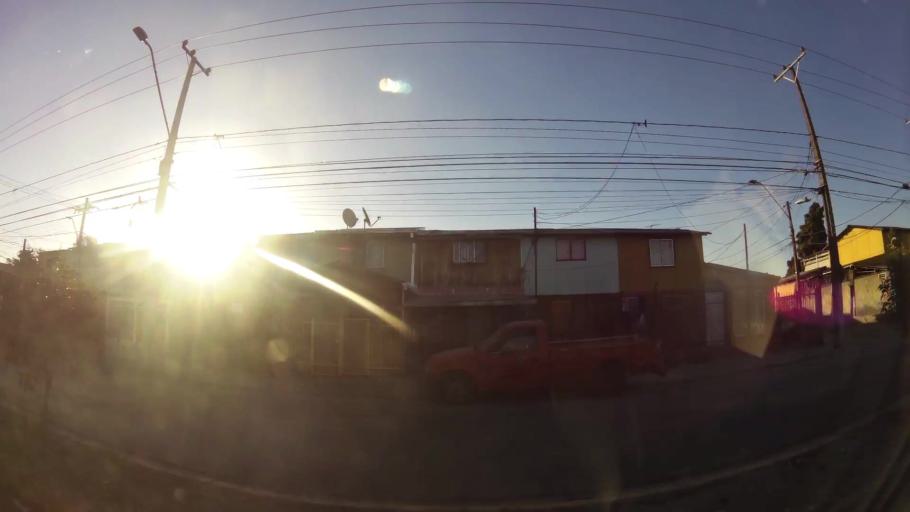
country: CL
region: Santiago Metropolitan
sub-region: Provincia de Maipo
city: San Bernardo
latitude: -33.5987
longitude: -70.6877
